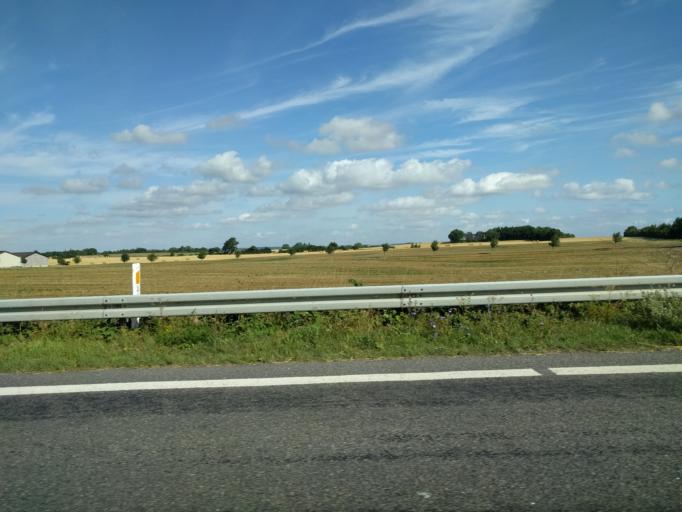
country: DK
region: Zealand
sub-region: Vordingborg Kommune
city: Stege
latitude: 54.9263
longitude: 12.1761
